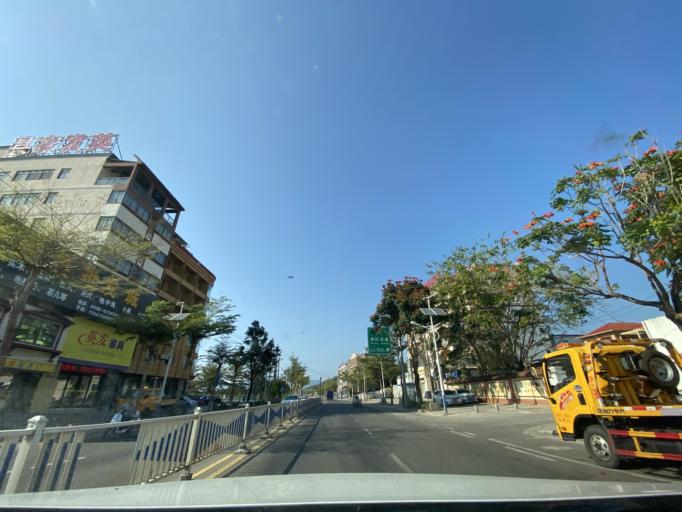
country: CN
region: Hainan
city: Yingzhou
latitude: 18.4301
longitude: 109.8537
